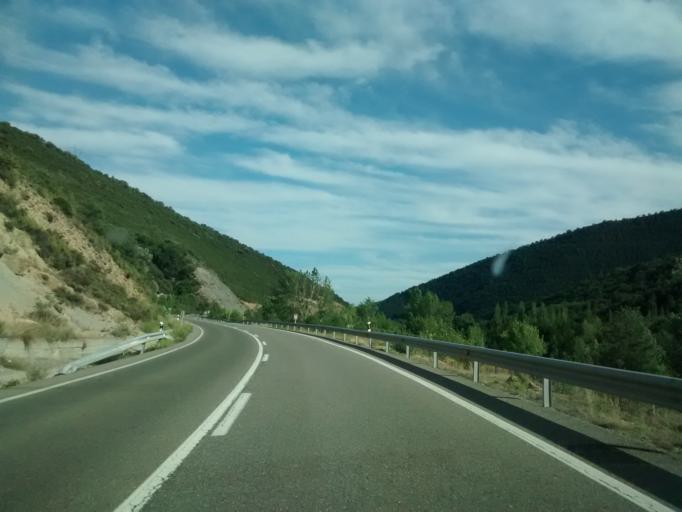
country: ES
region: Aragon
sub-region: Provincia de Huesca
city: Boltana
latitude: 42.4573
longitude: 0.0517
